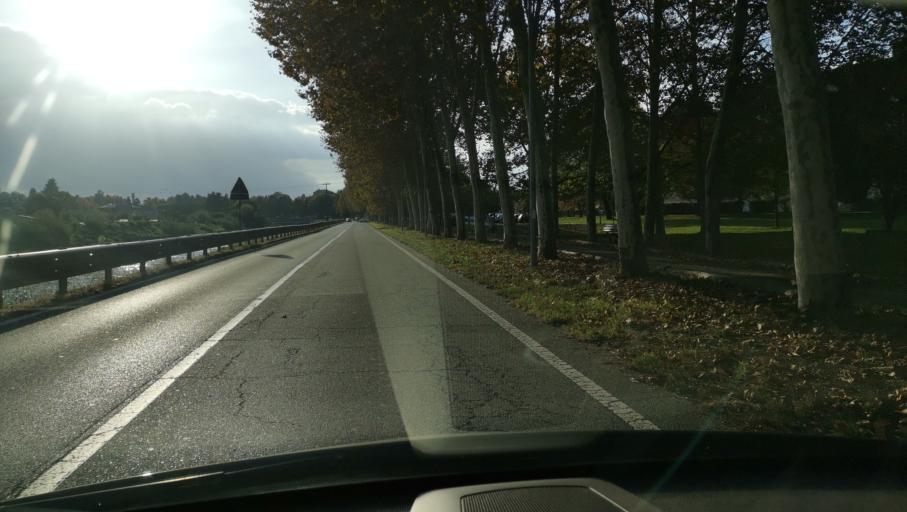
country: IT
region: Piedmont
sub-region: Provincia di Torino
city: Chivasso
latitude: 45.1906
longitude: 7.9038
